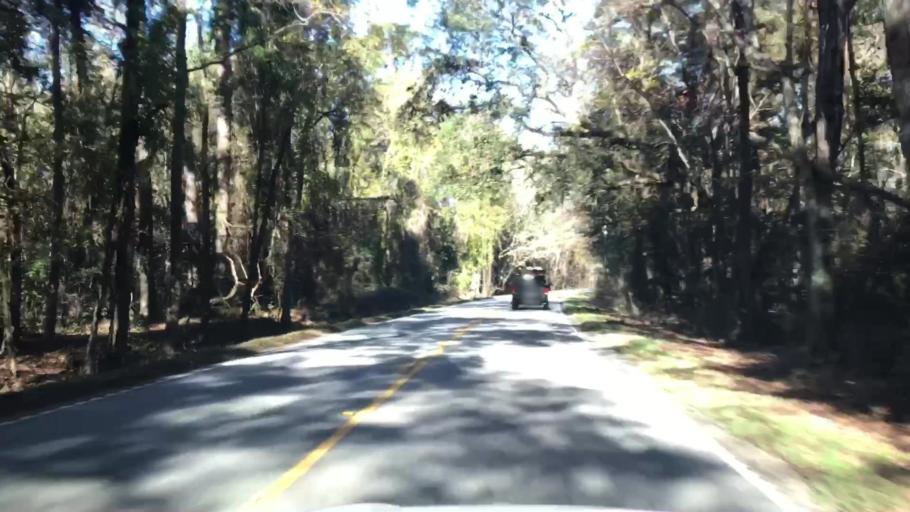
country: US
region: South Carolina
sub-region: Berkeley County
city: Ladson
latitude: 32.9041
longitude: -80.1458
